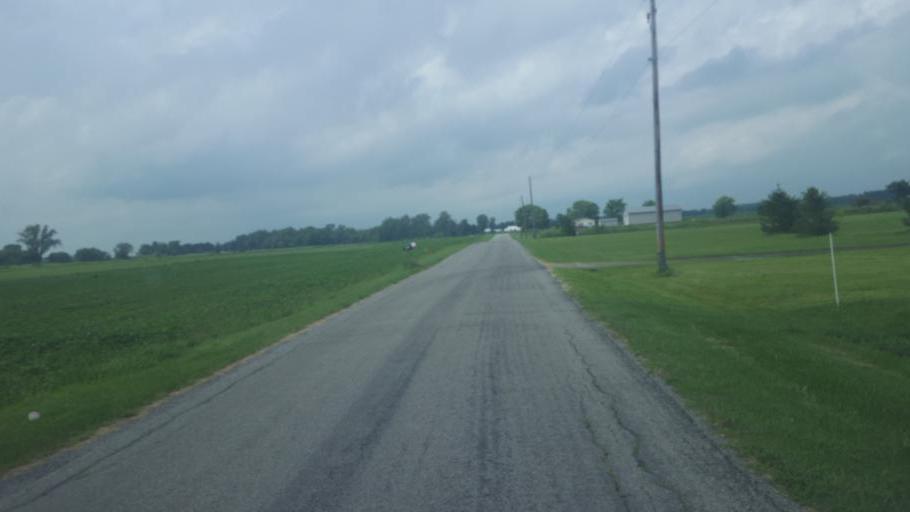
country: US
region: Ohio
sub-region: Union County
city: Richwood
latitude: 40.4846
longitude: -83.3155
